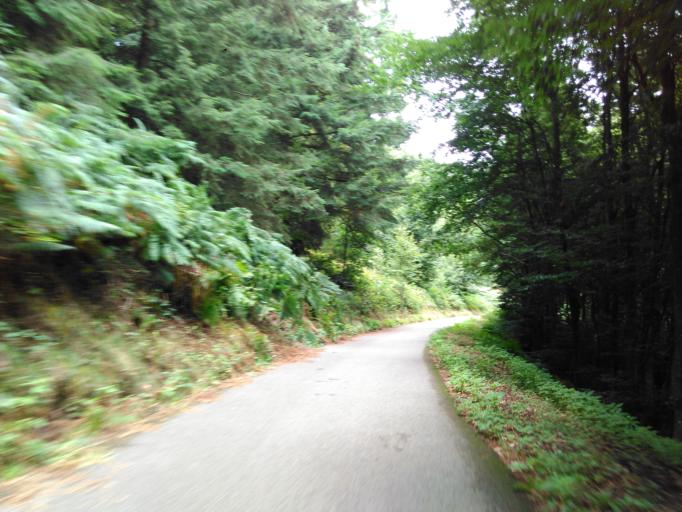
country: LU
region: Grevenmacher
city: Gonderange
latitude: 49.6673
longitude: 6.2293
